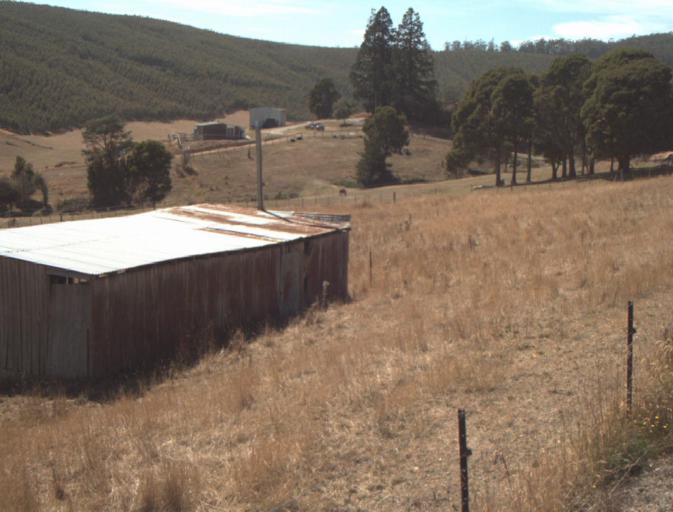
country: AU
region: Tasmania
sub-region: Launceston
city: Mayfield
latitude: -41.2362
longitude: 147.2567
